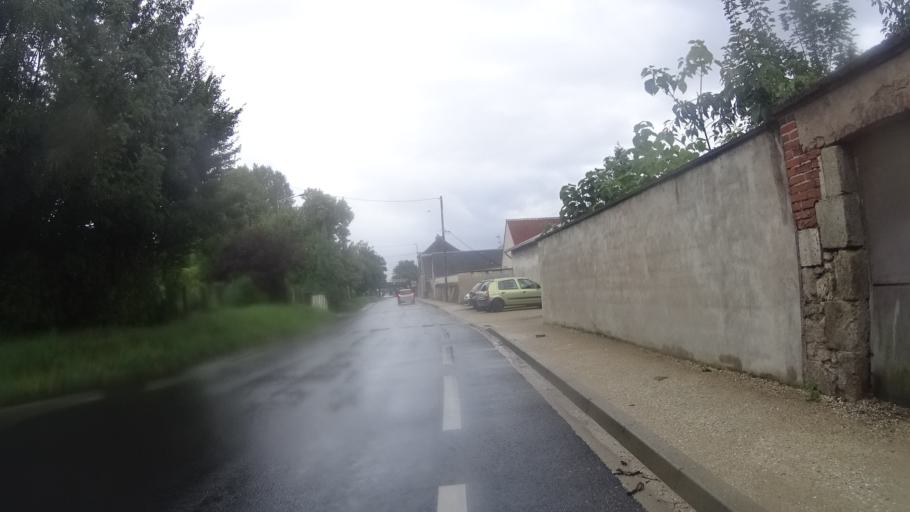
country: FR
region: Centre
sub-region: Departement du Loiret
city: Saint-Jean-le-Blanc
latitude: 47.8939
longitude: 1.9190
